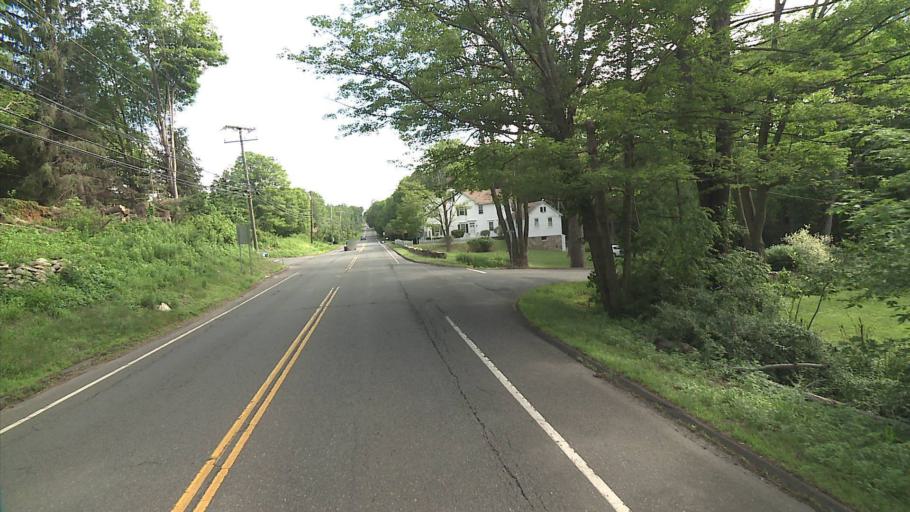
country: US
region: Connecticut
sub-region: New Haven County
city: Prospect
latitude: 41.4278
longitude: -72.9950
